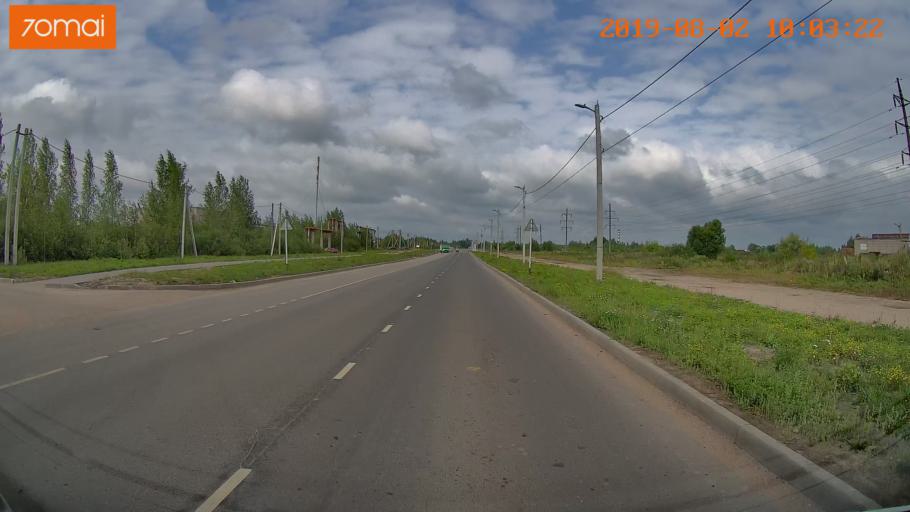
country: RU
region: Ivanovo
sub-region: Gorod Ivanovo
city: Ivanovo
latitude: 56.9663
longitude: 40.9426
